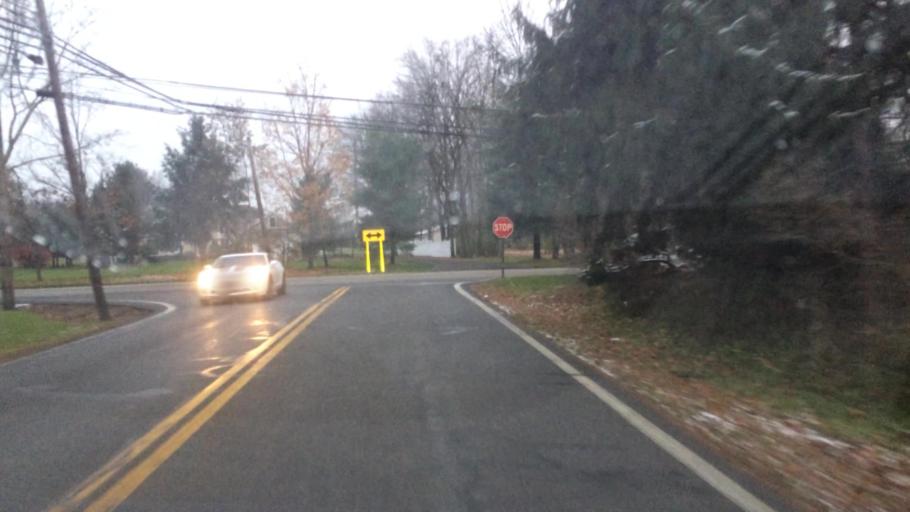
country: US
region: Ohio
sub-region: Cuyahoga County
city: Olmsted Falls
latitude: 41.3512
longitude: -81.9267
